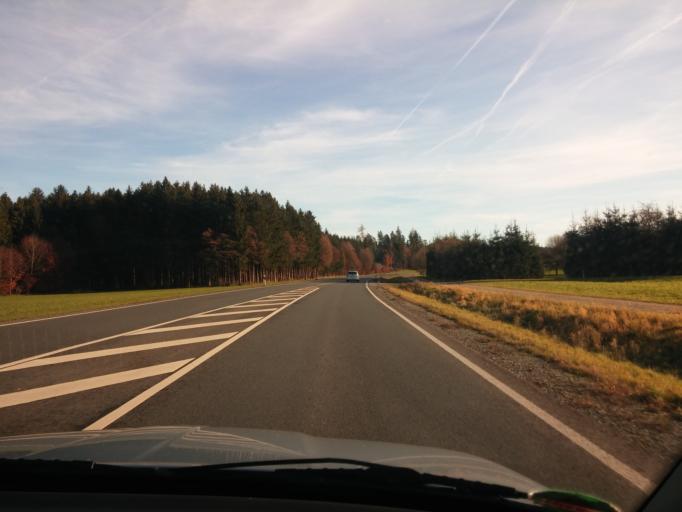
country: DE
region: Bavaria
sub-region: Upper Bavaria
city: Babensham
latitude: 48.0464
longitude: 12.2898
